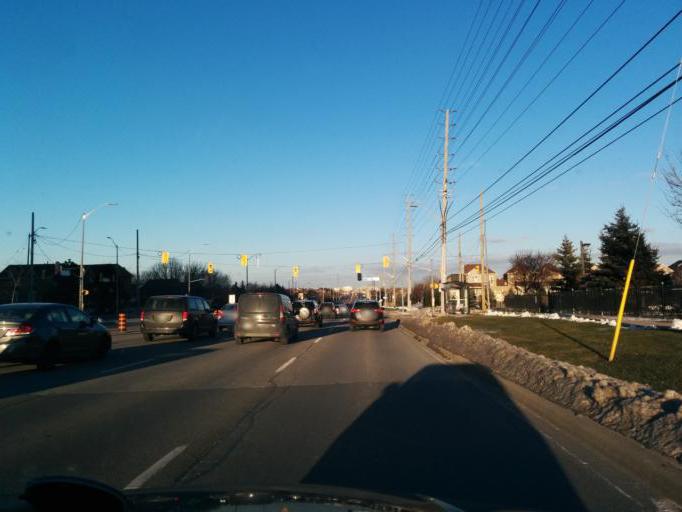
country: CA
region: Ontario
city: Mississauga
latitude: 43.6107
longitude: -79.6484
